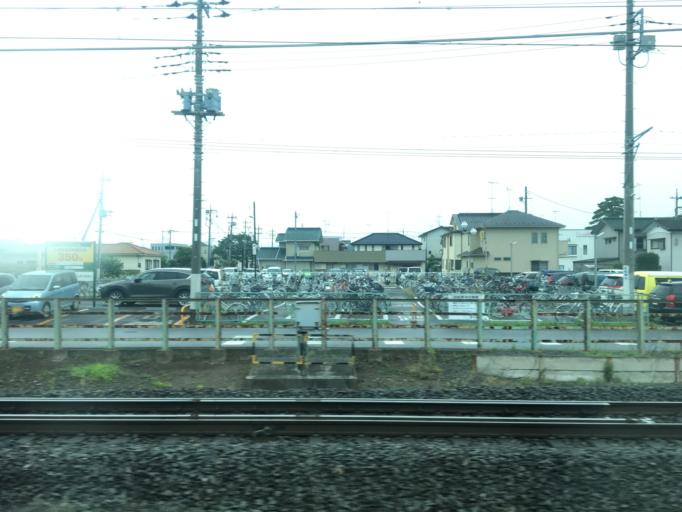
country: JP
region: Ibaraki
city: Koga
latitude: 36.2312
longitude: 139.7359
